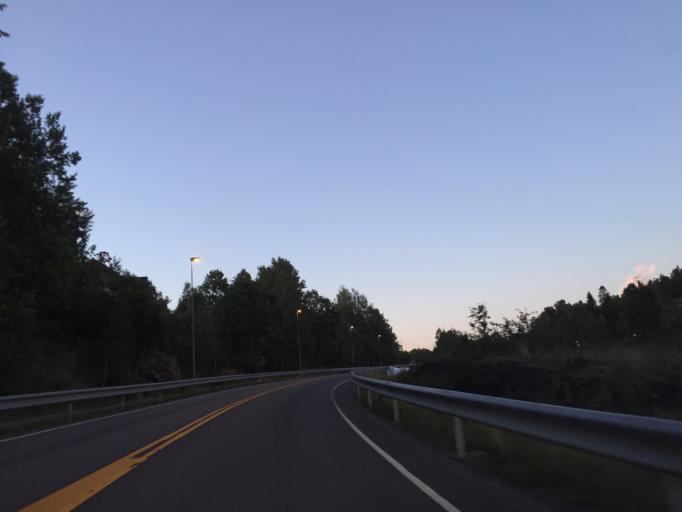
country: NO
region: Ostfold
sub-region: Moss
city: Moss
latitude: 59.5165
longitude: 10.6922
